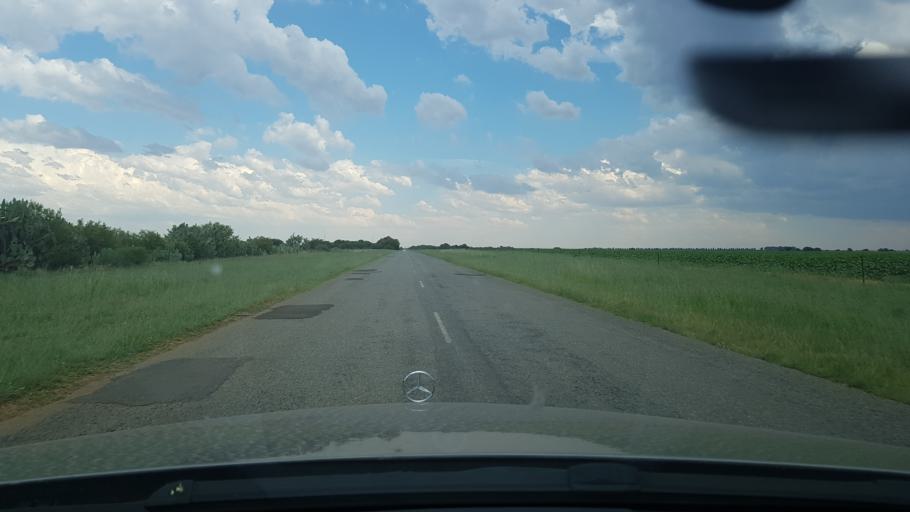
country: ZA
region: Orange Free State
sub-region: Lejweleputswa District Municipality
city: Hoopstad
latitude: -27.9211
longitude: 25.6860
